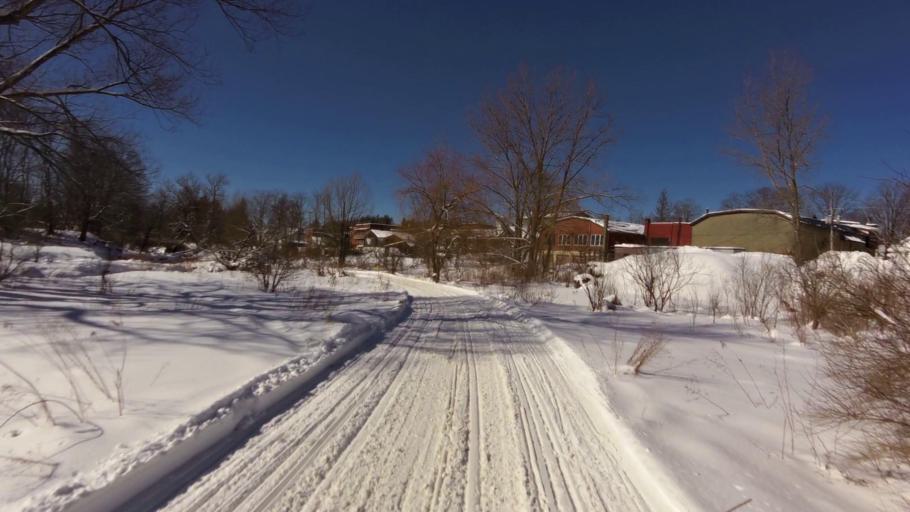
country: US
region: New York
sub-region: Chautauqua County
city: Mayville
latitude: 42.1584
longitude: -79.5935
